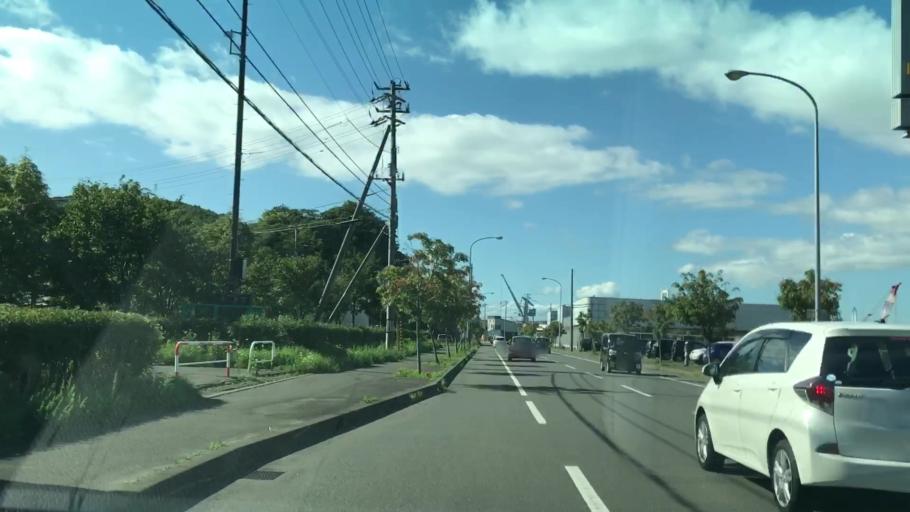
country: JP
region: Hokkaido
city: Muroran
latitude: 42.3321
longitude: 140.9639
